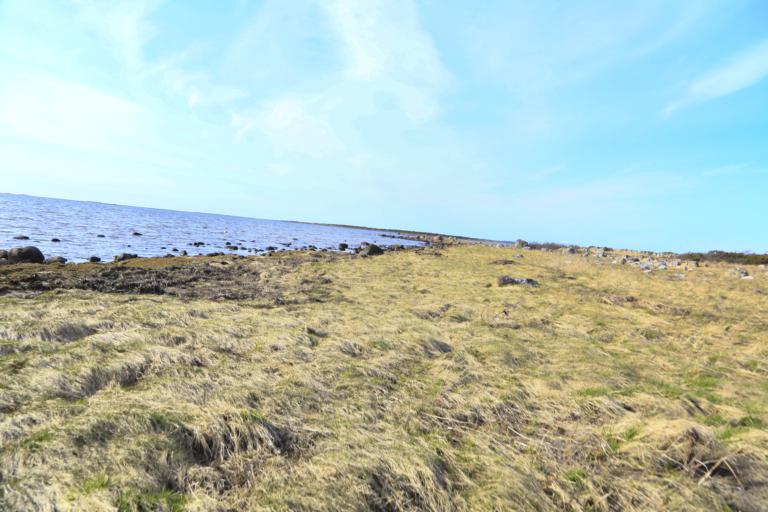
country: SE
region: Halland
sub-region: Varbergs Kommun
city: Varberg
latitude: 57.1284
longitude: 12.2124
